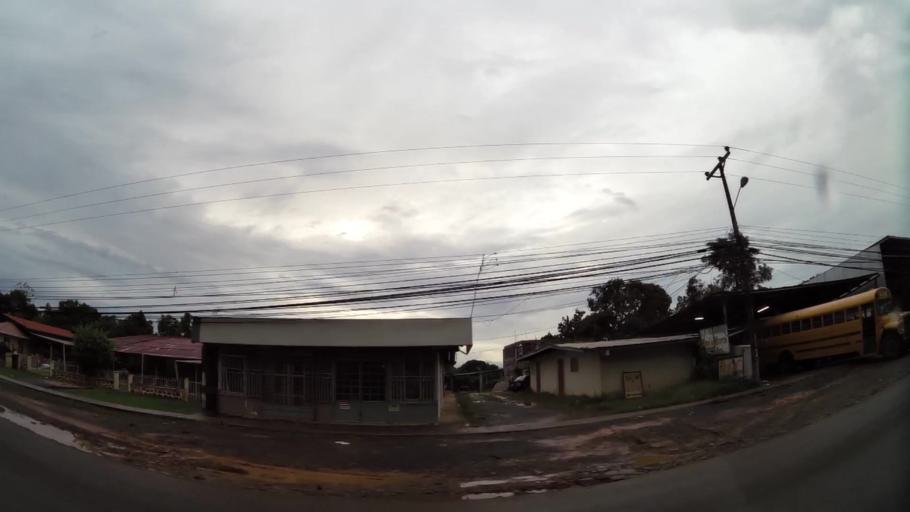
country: PA
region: Veraguas
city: Santiago de Veraguas
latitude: 8.1172
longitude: -80.9673
